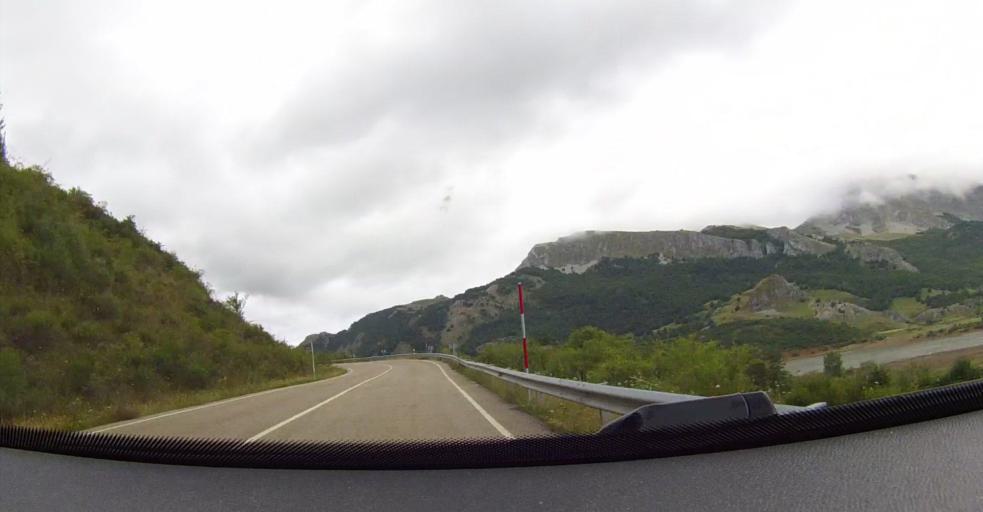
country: ES
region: Castille and Leon
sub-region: Provincia de Leon
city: Buron
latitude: 43.0238
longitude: -5.0441
